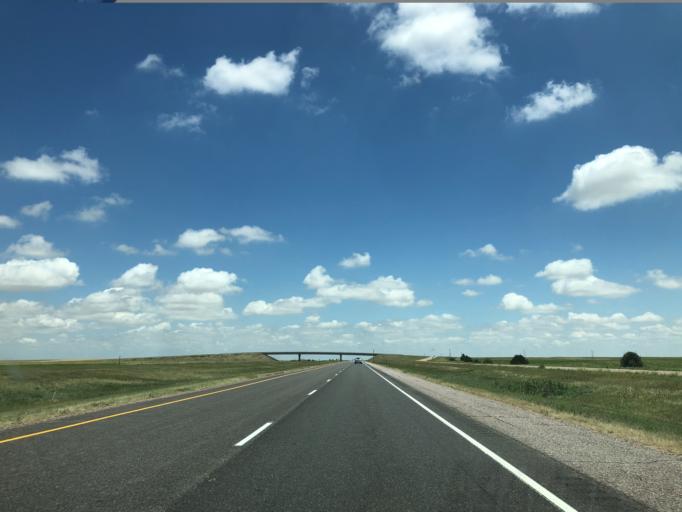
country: US
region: Colorado
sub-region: Lincoln County
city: Hugo
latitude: 39.2859
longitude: -103.1821
